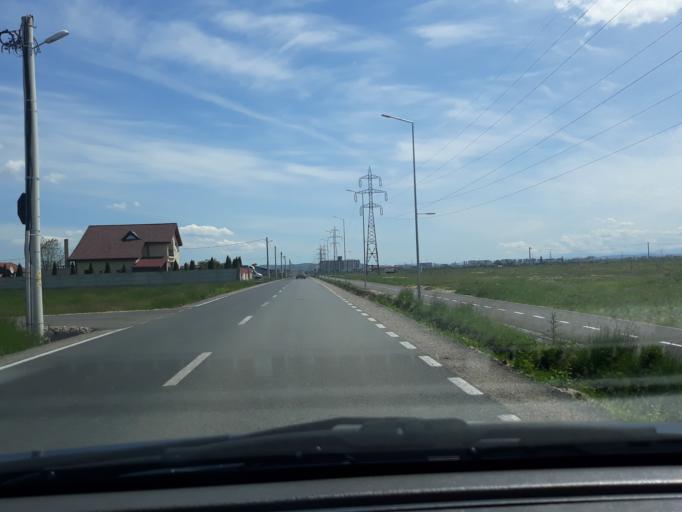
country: RO
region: Bihor
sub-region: Comuna Santandrei
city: Santandrei
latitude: 47.0675
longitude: 21.8643
